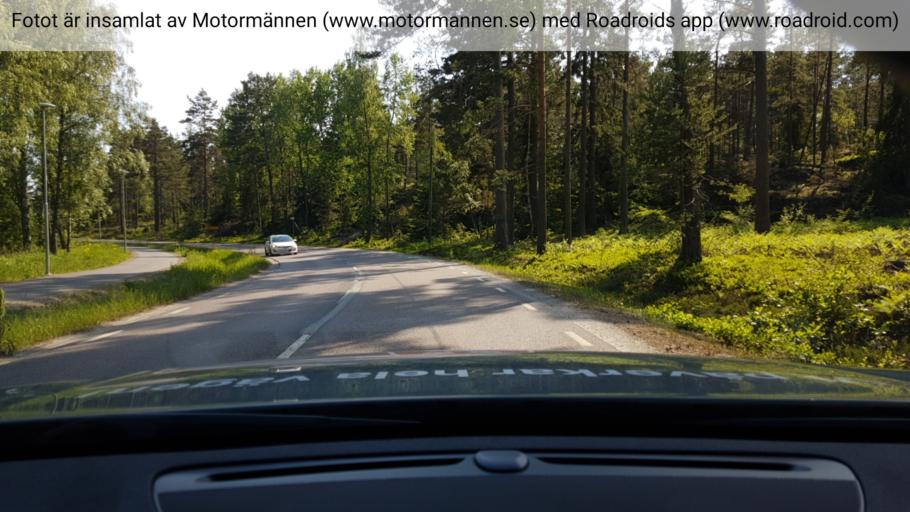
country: SE
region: Stockholm
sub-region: Varmdo Kommun
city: Mortnas
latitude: 59.2760
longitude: 18.4249
